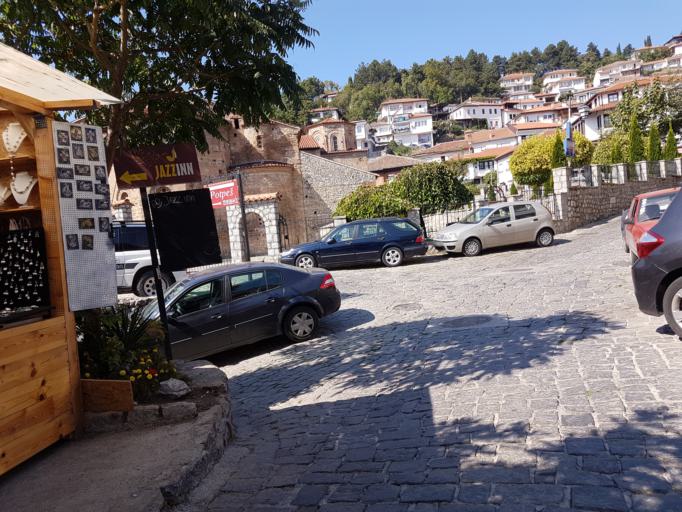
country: MK
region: Ohrid
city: Ohrid
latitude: 41.1122
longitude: 20.7950
